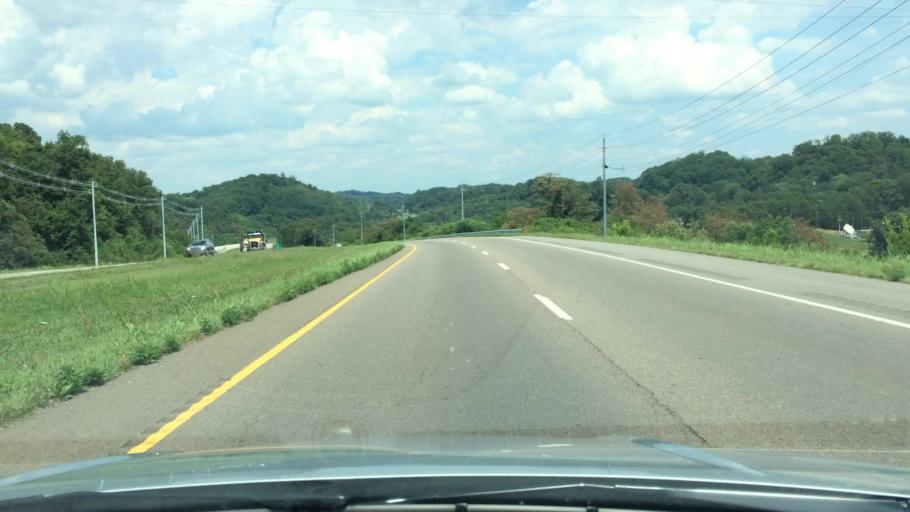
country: US
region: Tennessee
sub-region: Hamblen County
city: Morristown
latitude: 36.1891
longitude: -83.2864
